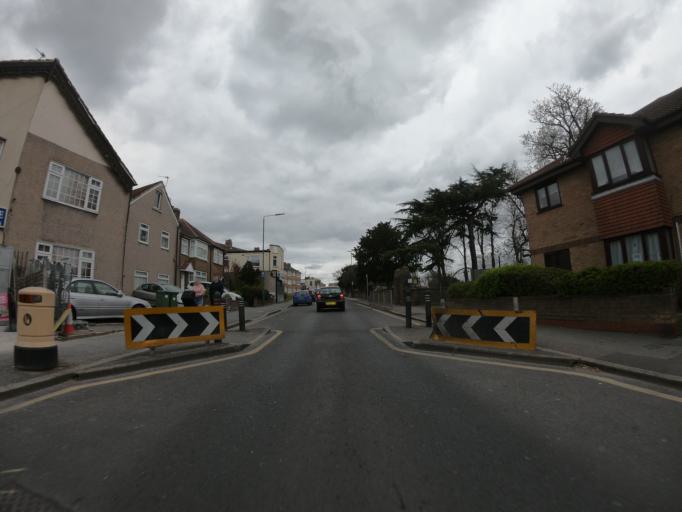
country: GB
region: England
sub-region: Greater London
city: Belvedere
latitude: 51.4826
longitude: 0.1442
